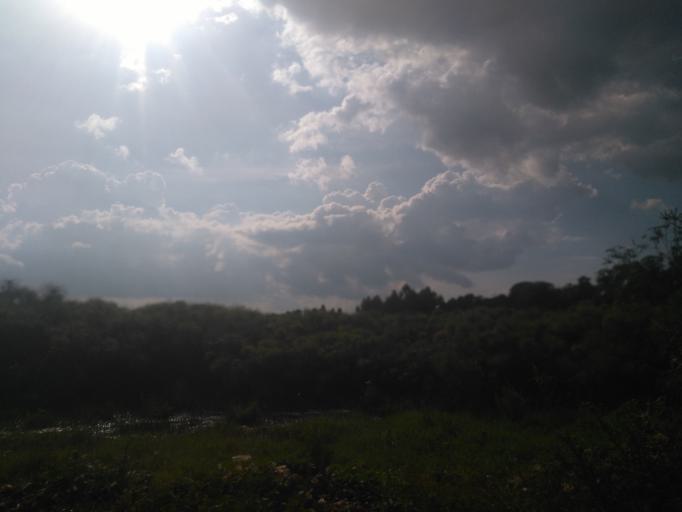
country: UG
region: Central Region
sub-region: Wakiso District
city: Wakiso
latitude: 0.3132
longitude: 32.4431
